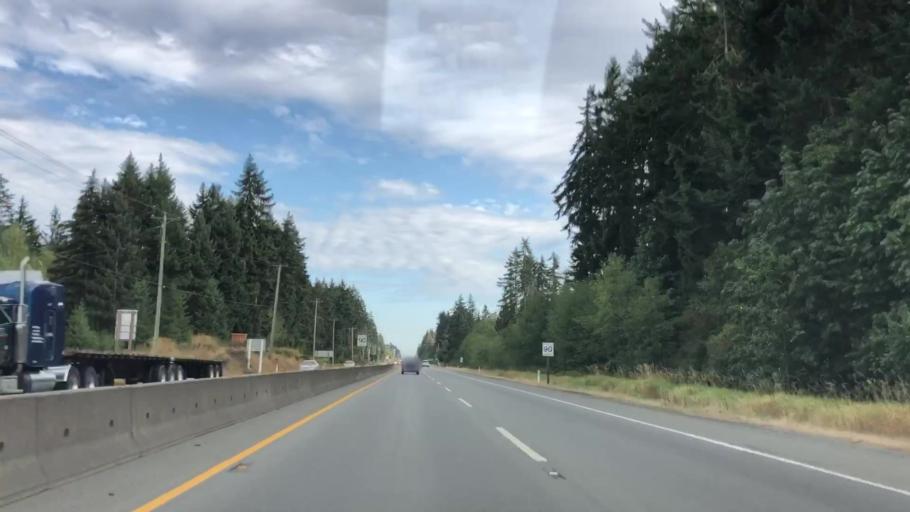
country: CA
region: British Columbia
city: Duncan
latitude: 48.7053
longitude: -123.6046
